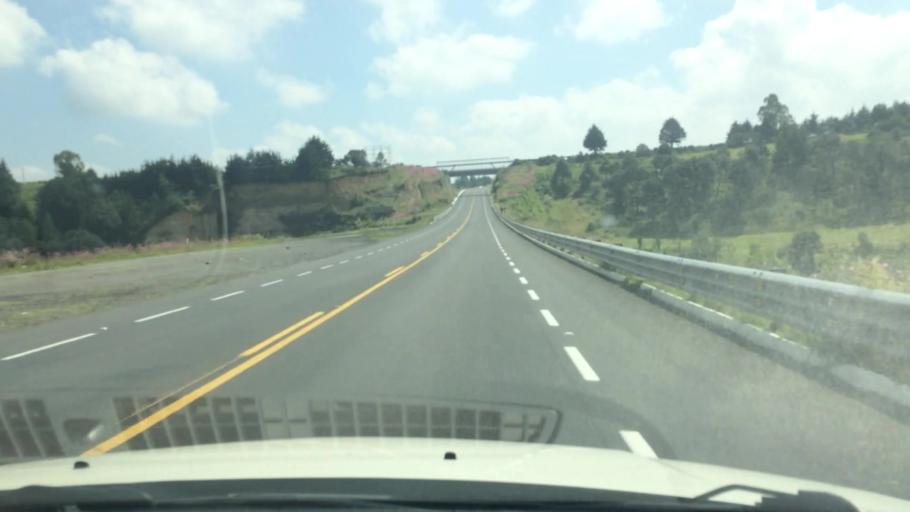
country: MX
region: Mexico
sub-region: Villa Victoria
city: Colonia Doctor Gustavo Baz
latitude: 19.3767
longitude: -99.8870
